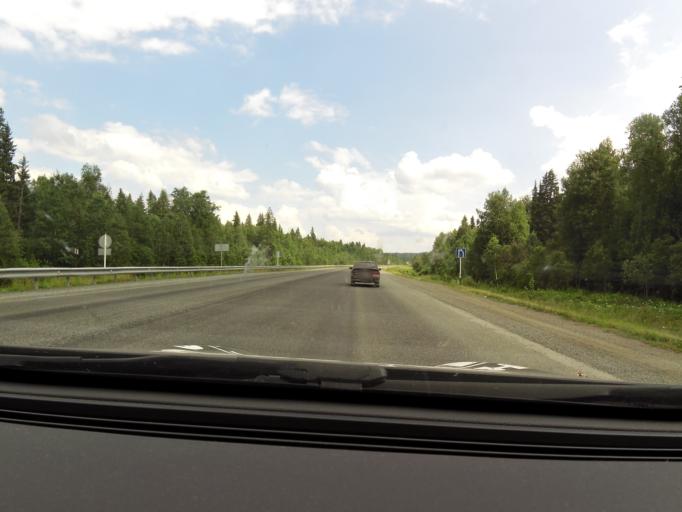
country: RU
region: Sverdlovsk
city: Arti
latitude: 56.7943
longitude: 58.4869
